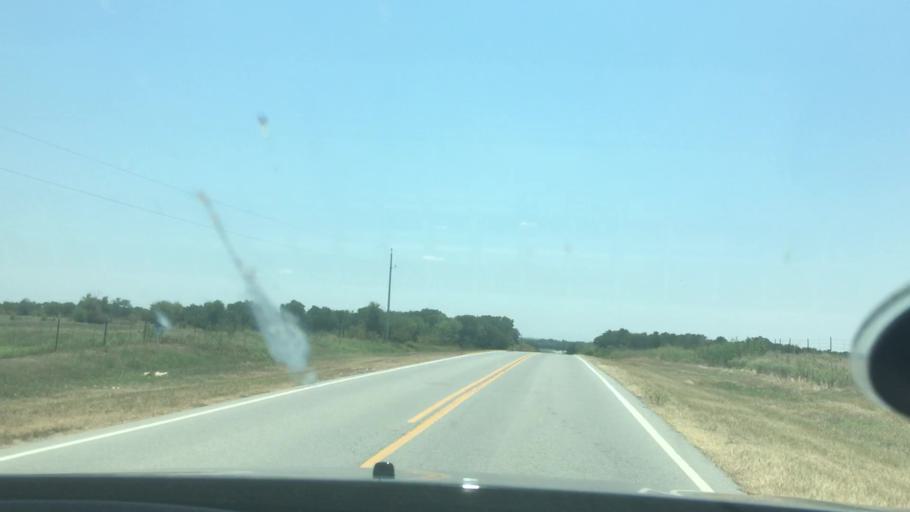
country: US
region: Oklahoma
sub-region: Coal County
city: Coalgate
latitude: 34.5627
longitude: -96.4069
